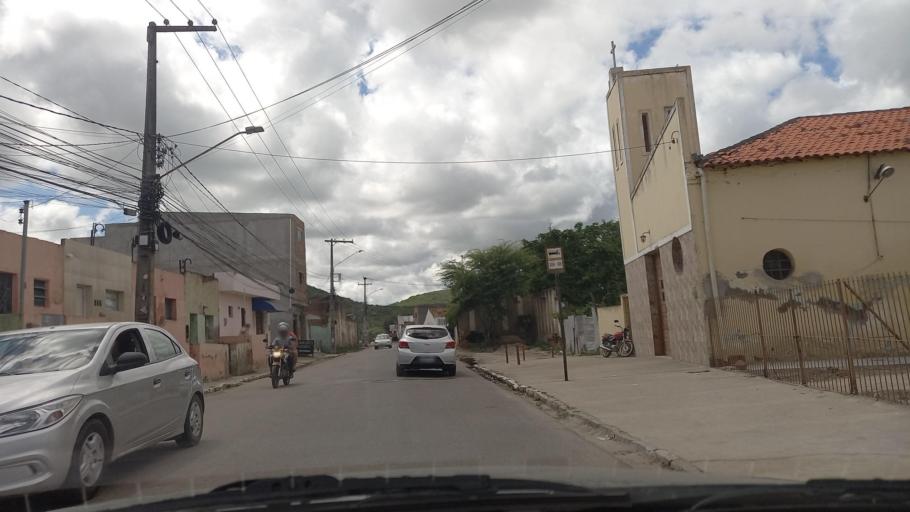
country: BR
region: Pernambuco
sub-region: Caruaru
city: Caruaru
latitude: -8.2793
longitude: -35.9454
